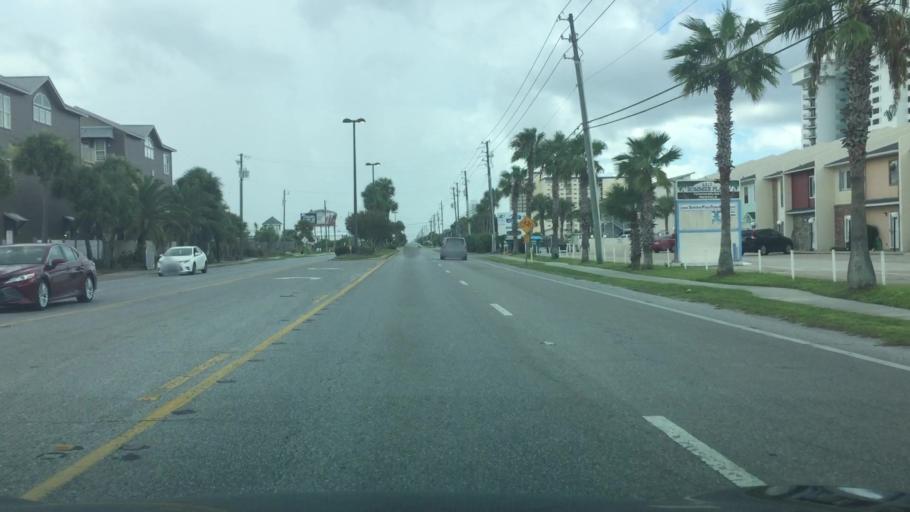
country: US
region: Florida
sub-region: Bay County
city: Lower Grand Lagoon
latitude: 30.1512
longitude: -85.7653
